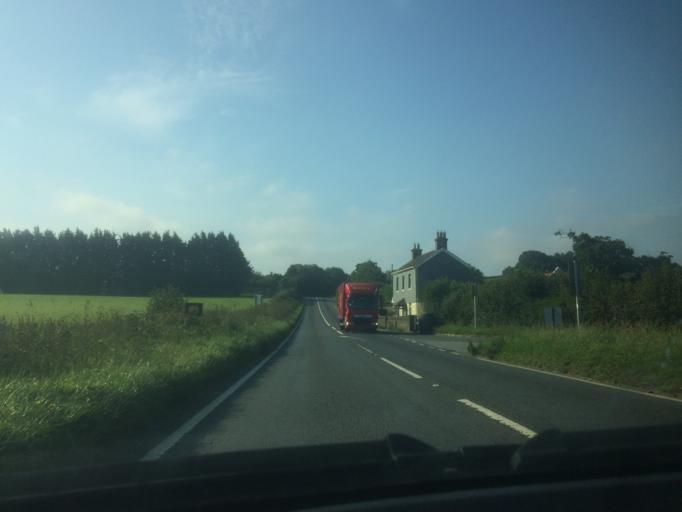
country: GB
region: England
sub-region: Cornwall
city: Pillaton
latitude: 50.4450
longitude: -4.2561
